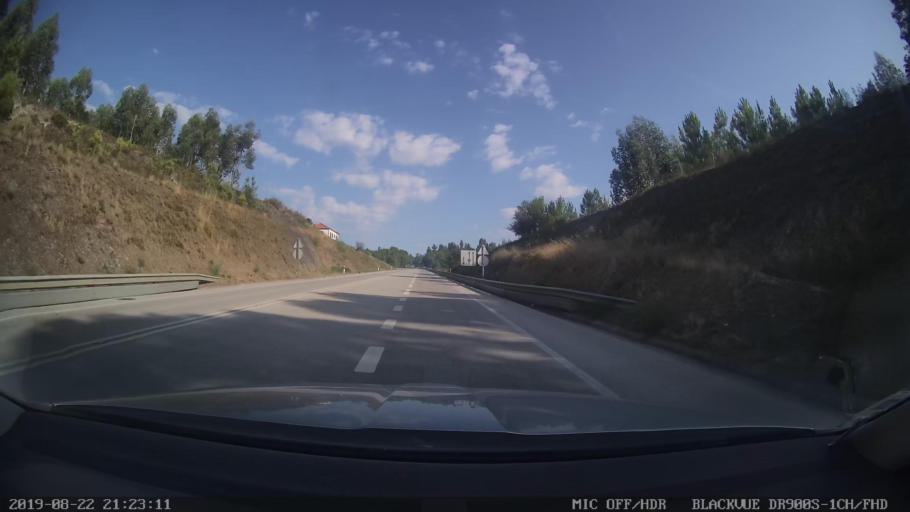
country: PT
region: Castelo Branco
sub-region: Serta
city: Serta
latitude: 39.8269
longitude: -8.1073
